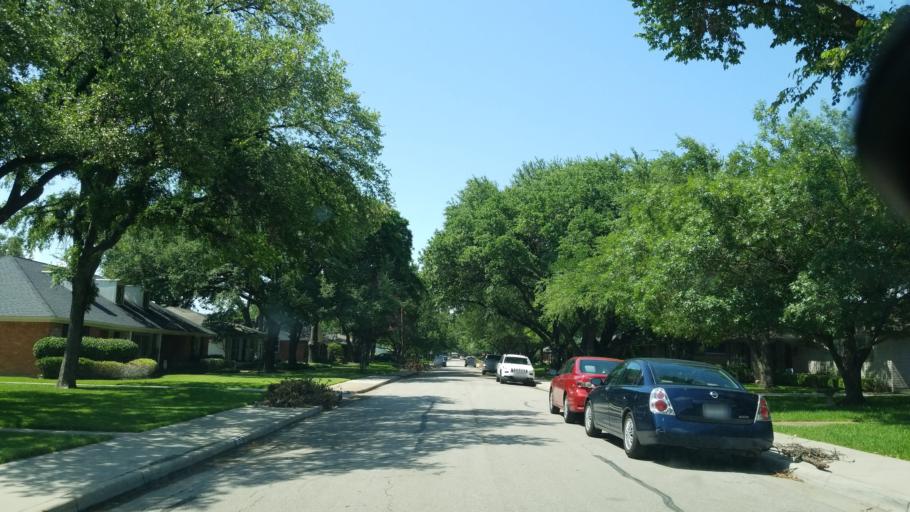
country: US
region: Texas
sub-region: Dallas County
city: Farmers Branch
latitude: 32.8910
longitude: -96.8639
